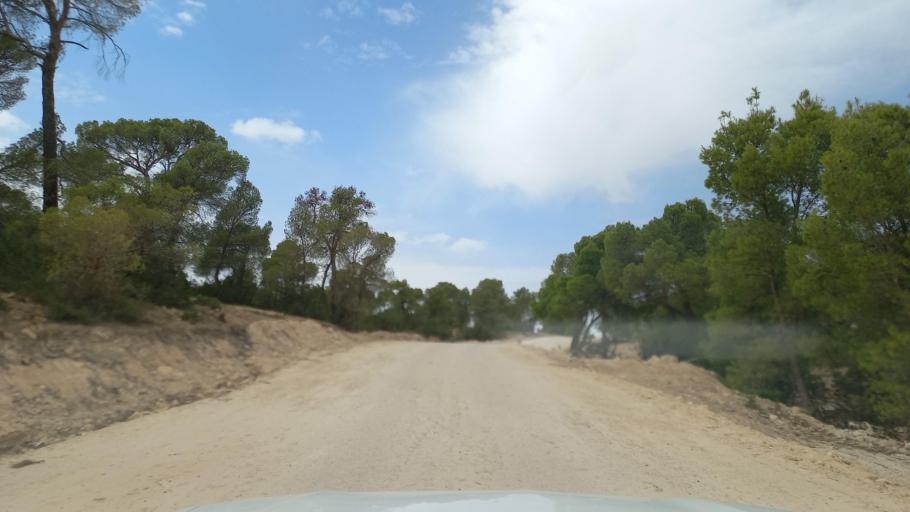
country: TN
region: Al Qasrayn
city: Kasserine
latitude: 35.3813
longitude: 8.8822
